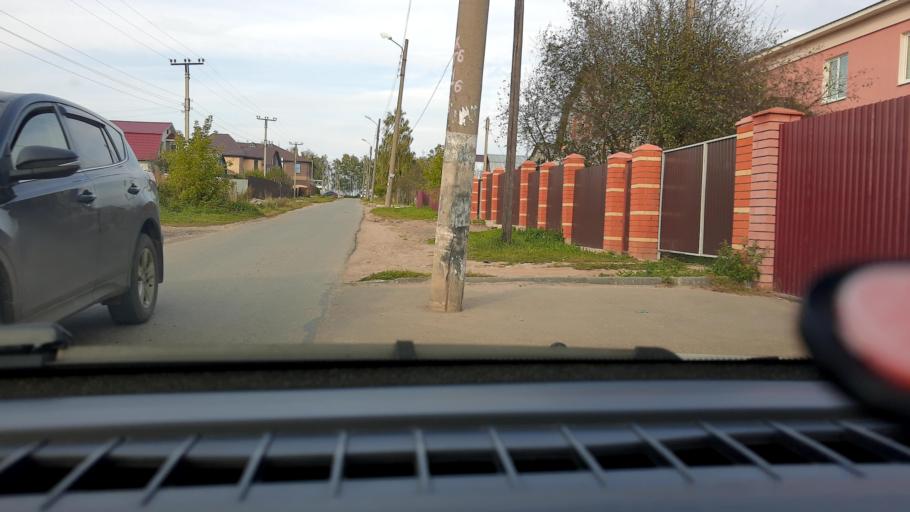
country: RU
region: Nizjnij Novgorod
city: Nizhniy Novgorod
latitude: 56.2126
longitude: 43.9585
